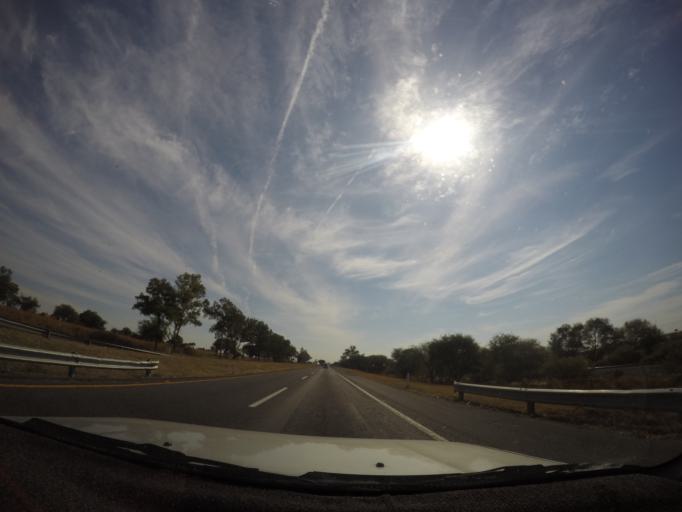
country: MX
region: Jalisco
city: La Barca
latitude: 20.3220
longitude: -102.5274
